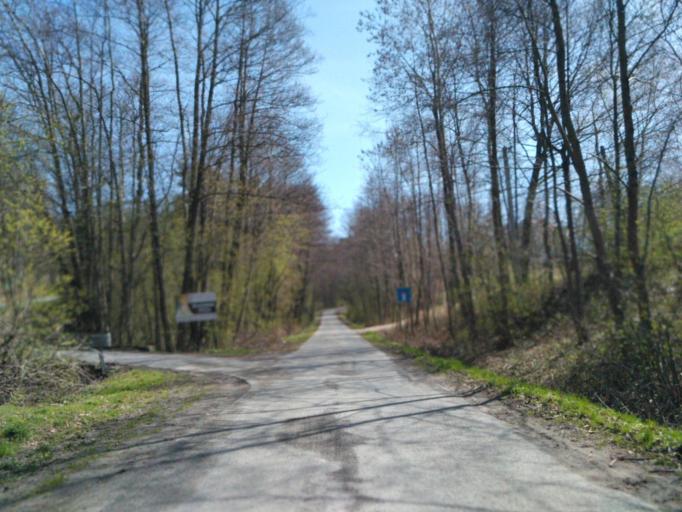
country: PL
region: Subcarpathian Voivodeship
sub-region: Powiat strzyzowski
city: Babica
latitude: 49.9269
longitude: 21.8852
